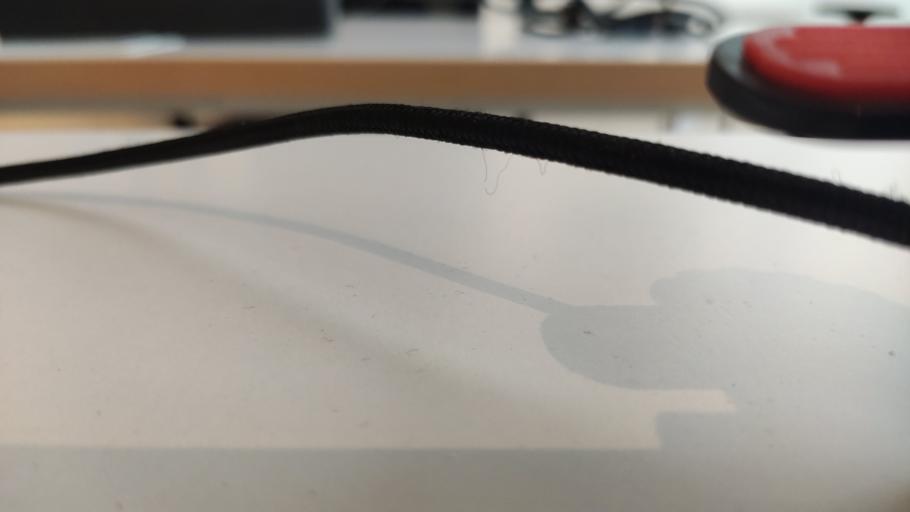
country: RU
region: Moskovskaya
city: Shevlyakovo
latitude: 56.3975
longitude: 36.8628
